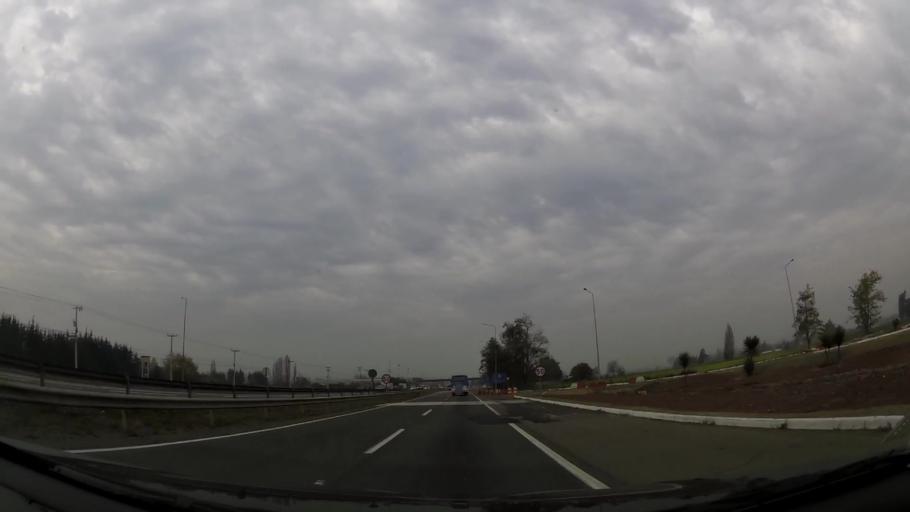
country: CL
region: Santiago Metropolitan
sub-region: Provincia de Chacabuco
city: Chicureo Abajo
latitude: -33.2327
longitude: -70.7603
